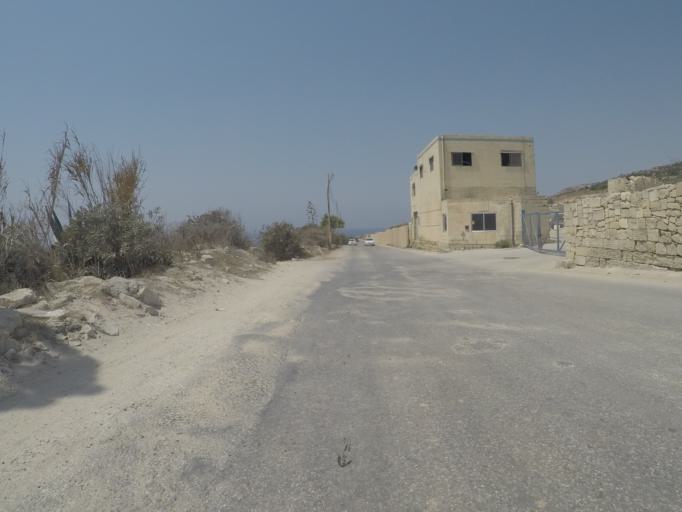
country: MT
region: Is-Siggiewi
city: Siggiewi
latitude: 35.8343
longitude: 14.4202
